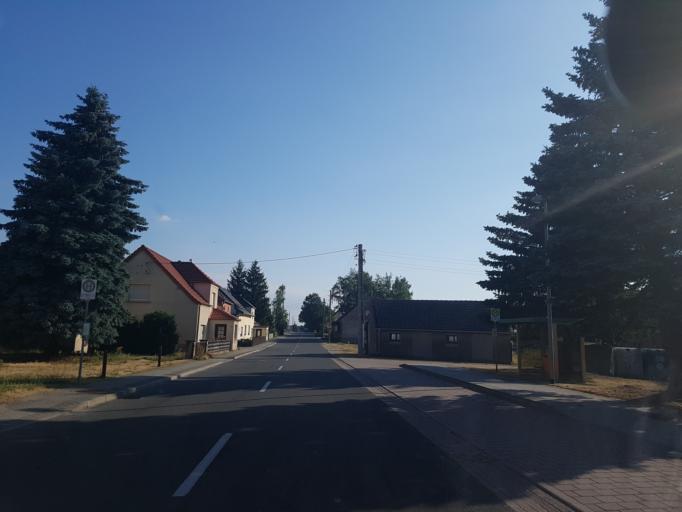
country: DE
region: Saxony-Anhalt
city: Seyda
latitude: 51.9053
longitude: 12.9406
